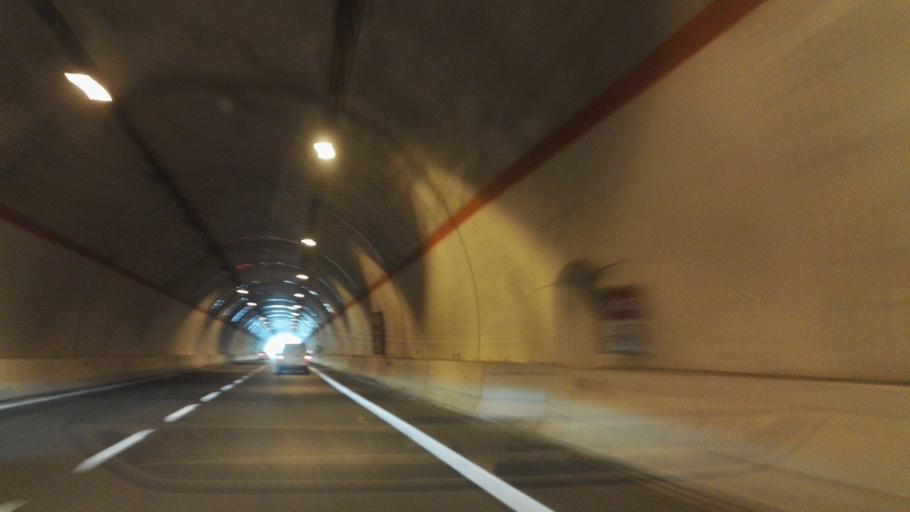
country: IT
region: Calabria
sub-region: Provincia di Catanzaro
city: Squillace Lido
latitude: 38.8072
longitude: 16.5572
